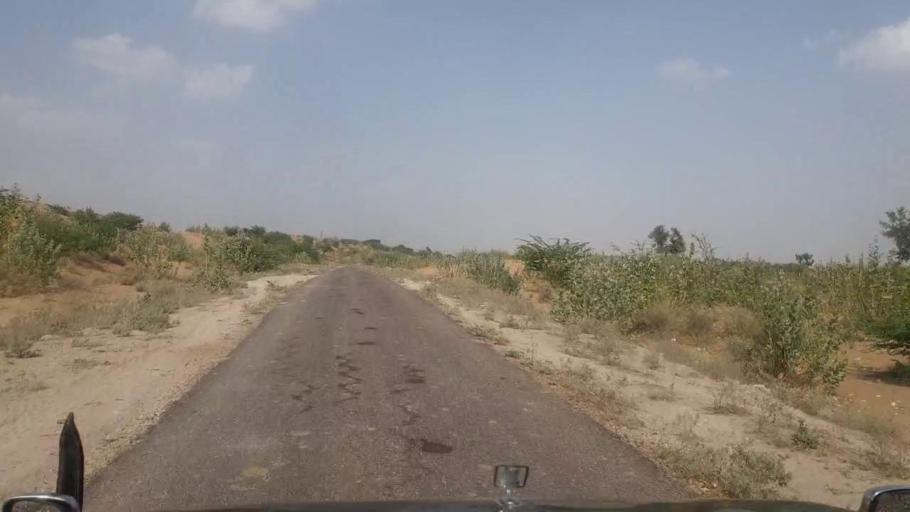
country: PK
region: Sindh
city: Islamkot
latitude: 25.2109
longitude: 70.2844
